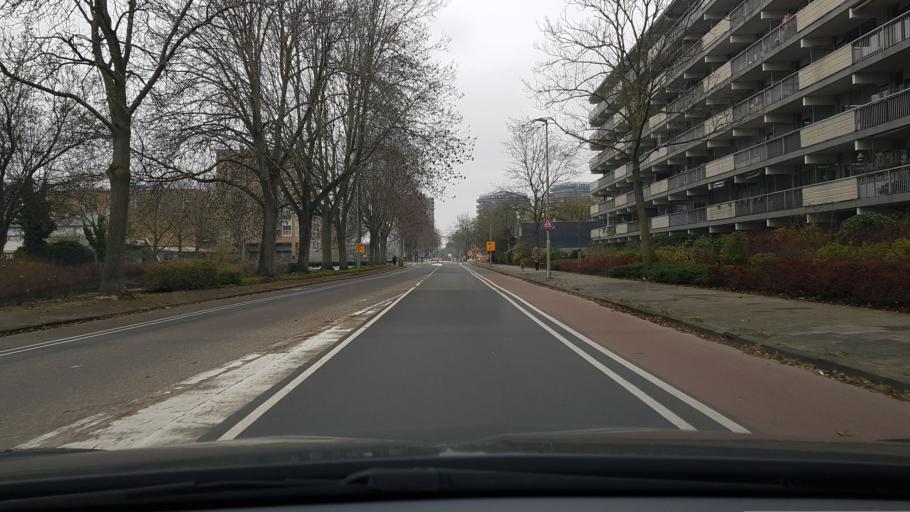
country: NL
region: North Holland
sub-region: Gemeente Haarlem
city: Haarlem
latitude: 52.3560
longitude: 4.6573
